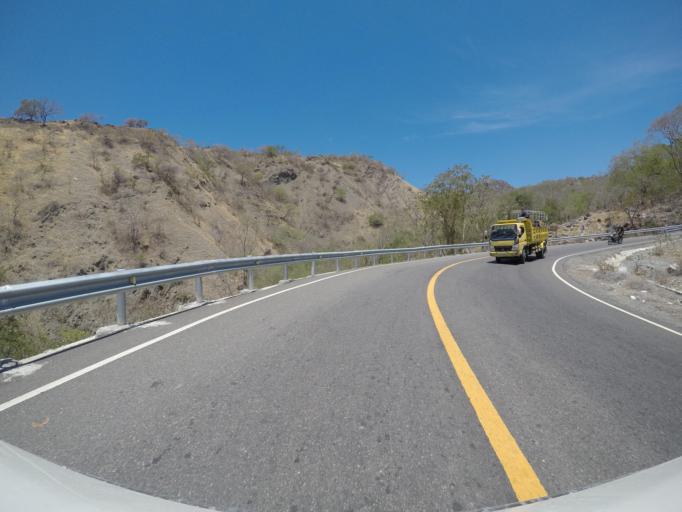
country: TL
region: Manatuto
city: Manatuto
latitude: -8.4934
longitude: 125.9649
